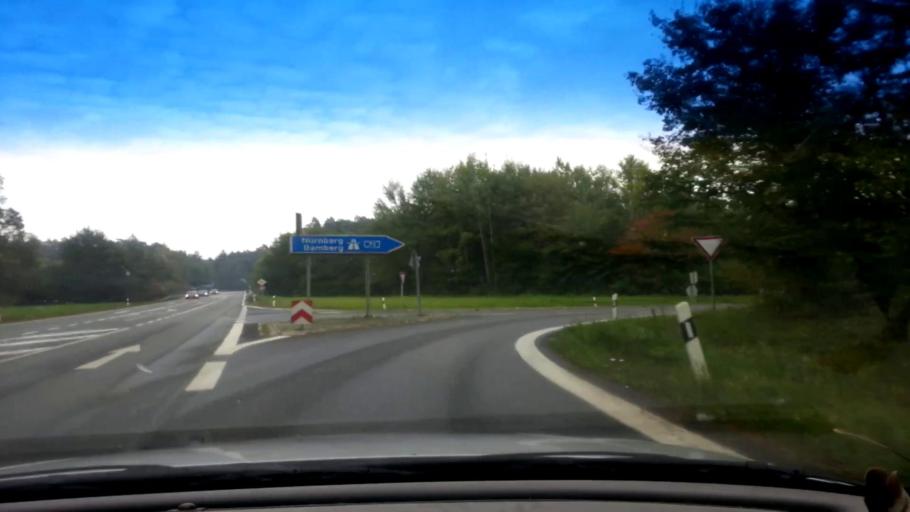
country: DE
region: Bavaria
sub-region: Upper Franconia
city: Zapfendorf
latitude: 50.0127
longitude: 10.9412
